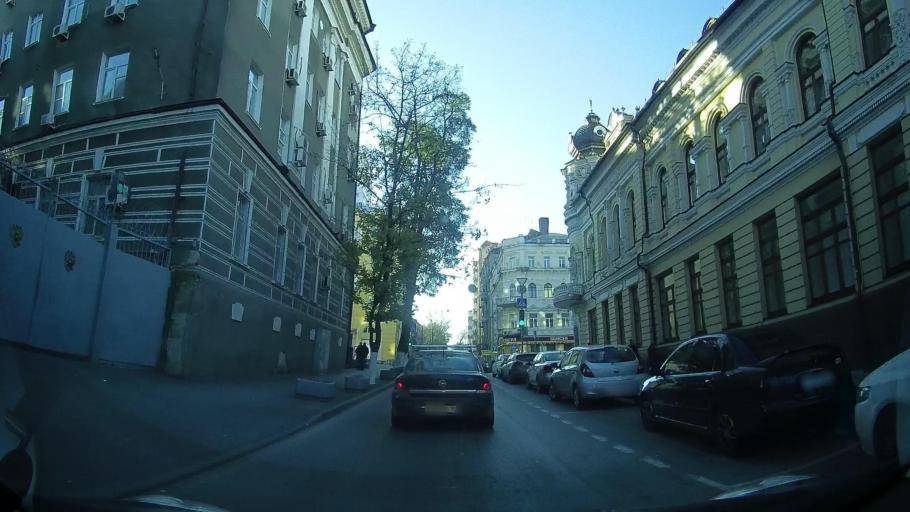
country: RU
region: Rostov
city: Rostov-na-Donu
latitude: 47.2195
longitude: 39.7024
